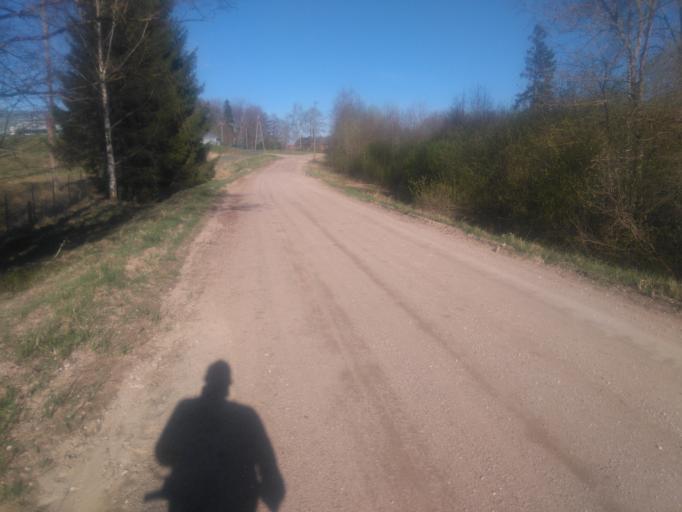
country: LV
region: Vecpiebalga
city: Vecpiebalga
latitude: 57.0192
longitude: 25.8471
